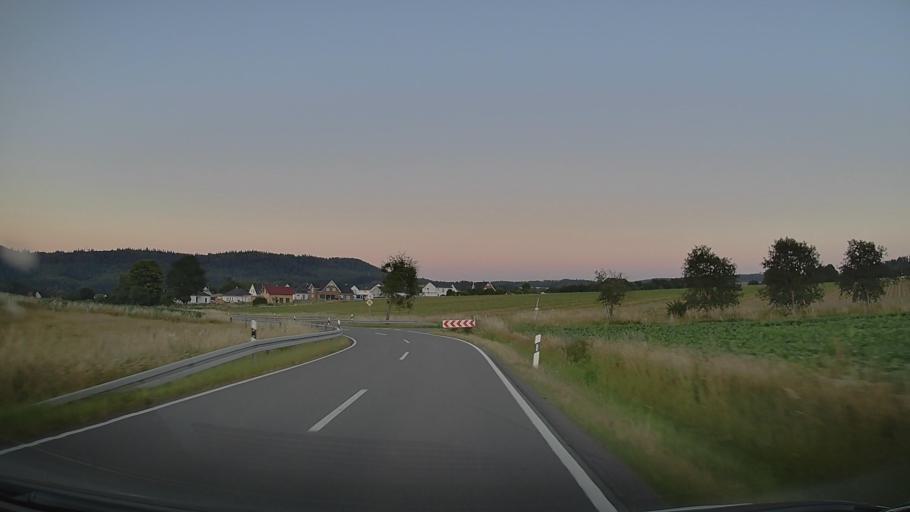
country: DE
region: Lower Saxony
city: Aerzen
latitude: 52.0121
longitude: 9.3259
